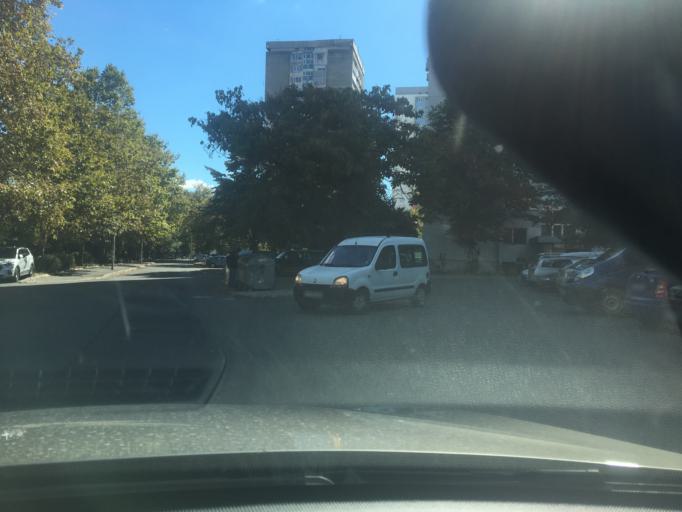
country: BG
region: Burgas
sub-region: Obshtina Burgas
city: Burgas
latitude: 42.5060
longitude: 27.4745
